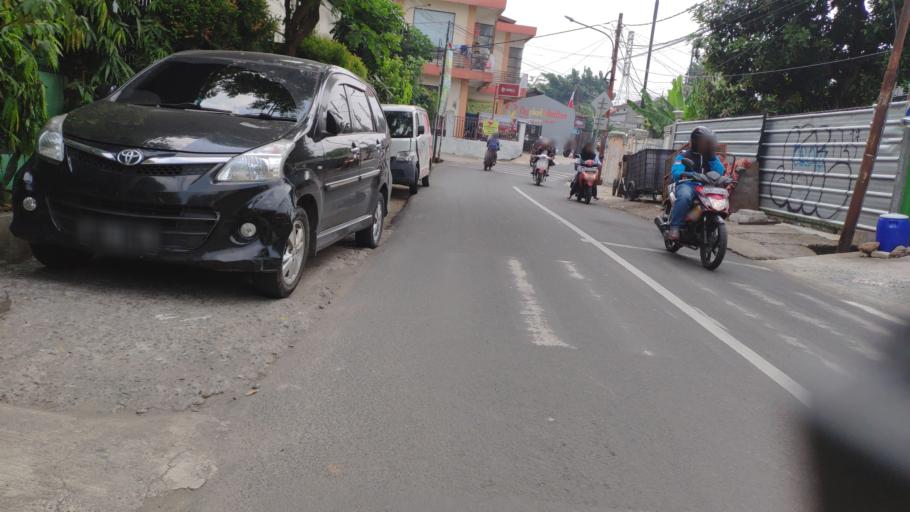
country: ID
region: West Java
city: Depok
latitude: -6.3266
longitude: 106.8263
